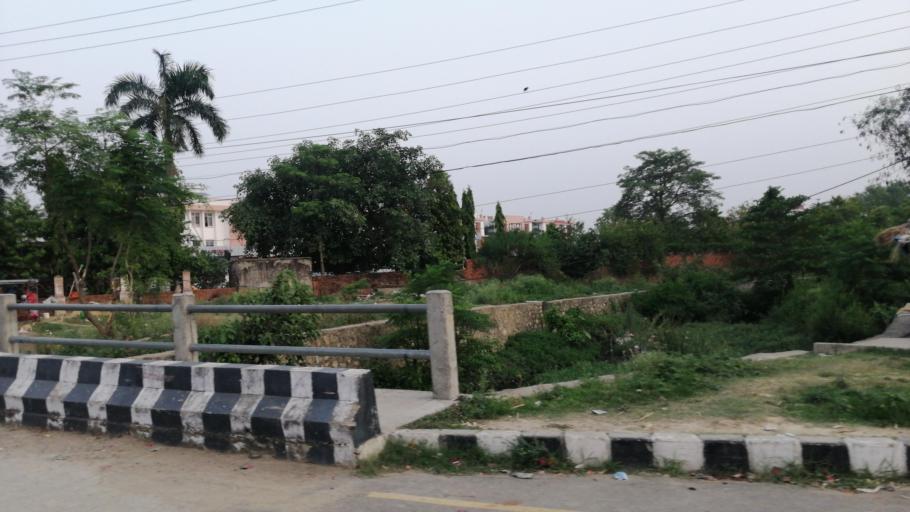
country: NP
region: Western Region
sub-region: Lumbini Zone
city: Bhairahawa
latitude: 27.4905
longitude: 83.4484
